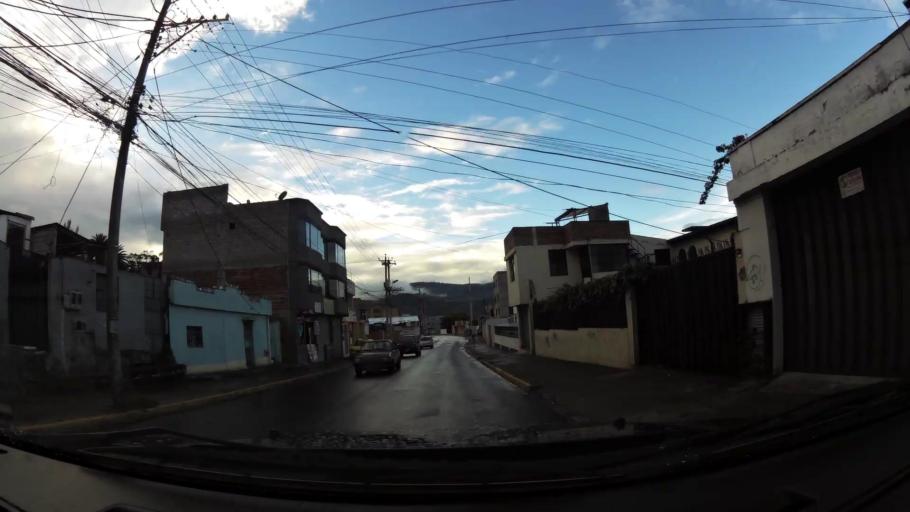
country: EC
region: Pichincha
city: Quito
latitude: -0.1136
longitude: -78.4998
